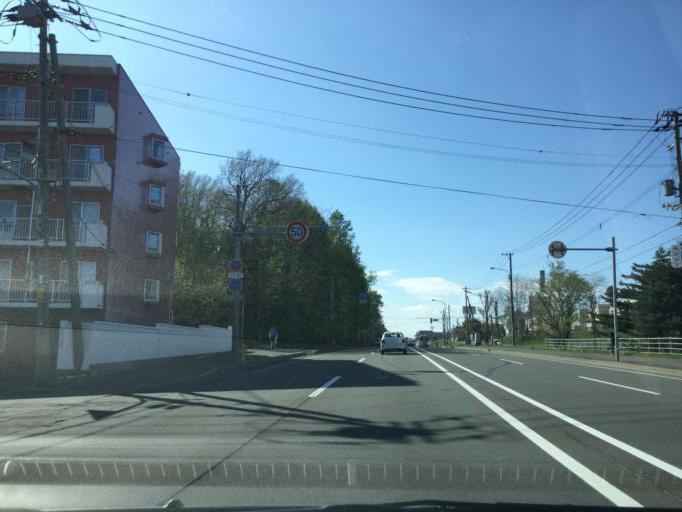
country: JP
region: Hokkaido
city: Sapporo
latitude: 43.0067
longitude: 141.4288
